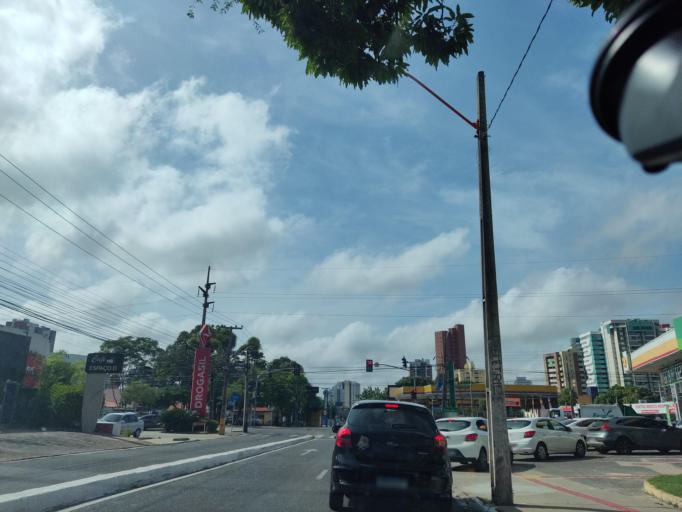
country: BR
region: Piaui
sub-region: Teresina
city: Teresina
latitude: -5.0697
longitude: -42.7832
